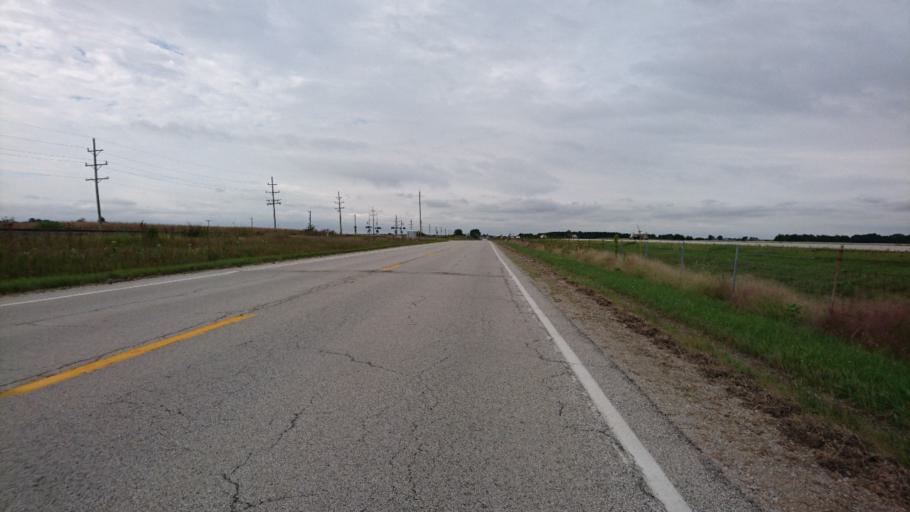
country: US
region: Illinois
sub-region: Livingston County
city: Dwight
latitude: 41.0601
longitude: -88.4691
